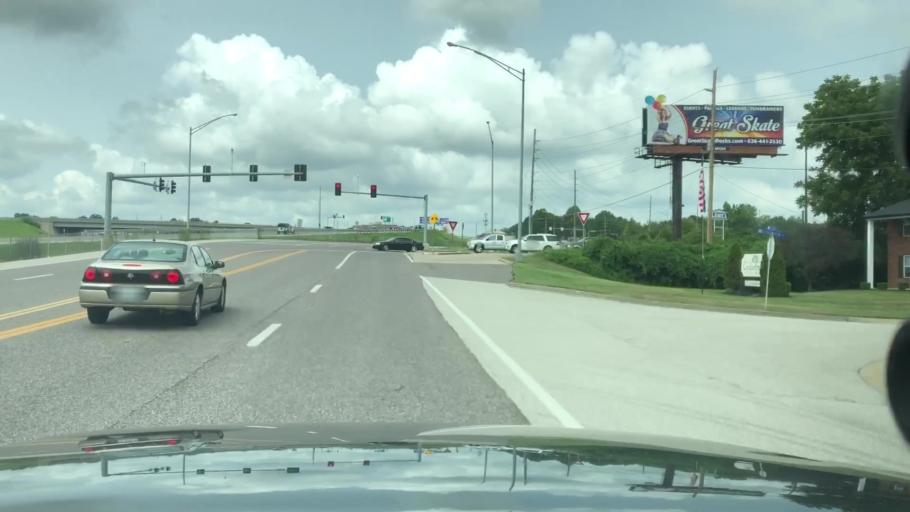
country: US
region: Missouri
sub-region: Saint Charles County
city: Saint Charles
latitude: 38.7867
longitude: -90.5303
